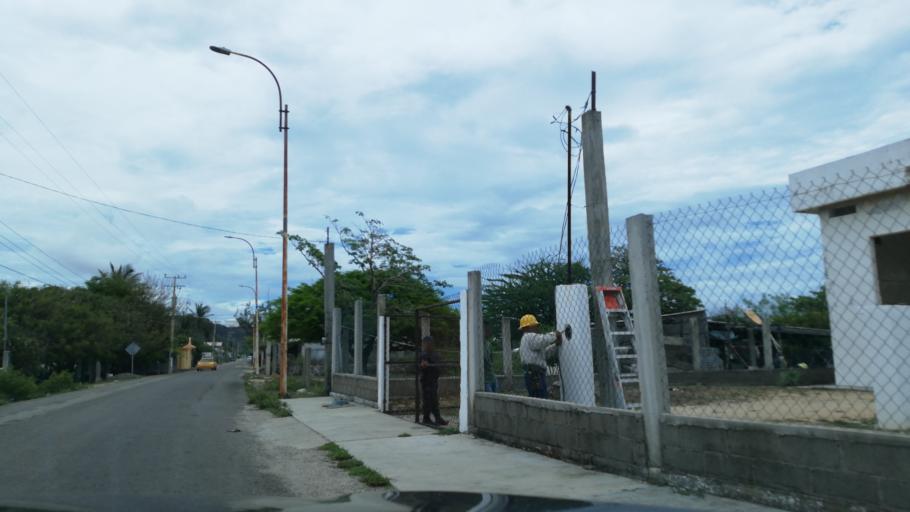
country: MX
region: Oaxaca
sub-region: Salina Cruz
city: Salina Cruz
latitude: 16.1623
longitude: -95.2268
